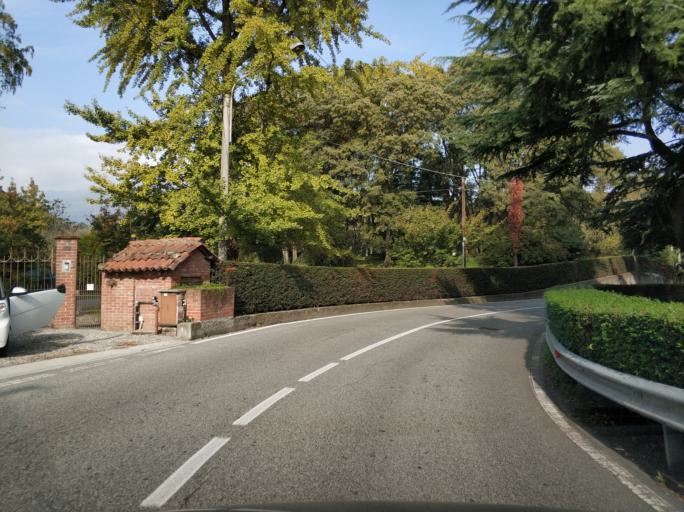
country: IT
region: Piedmont
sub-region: Provincia di Torino
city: Ivrea
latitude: 45.4788
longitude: 7.8795
